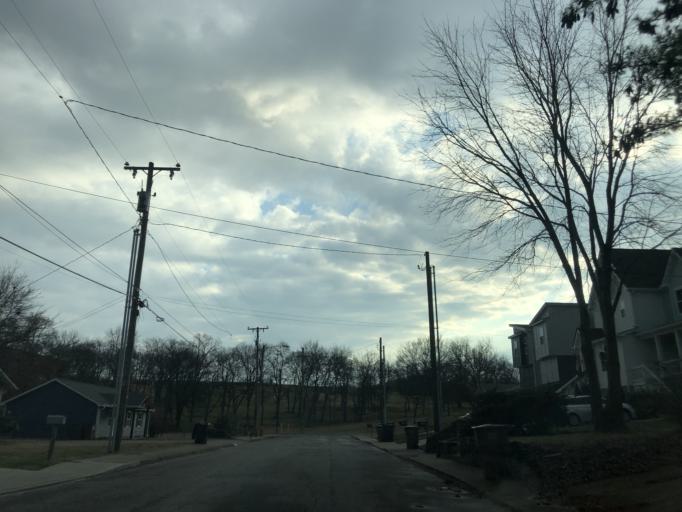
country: US
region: Tennessee
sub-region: Davidson County
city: Nashville
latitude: 36.1995
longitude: -86.7279
